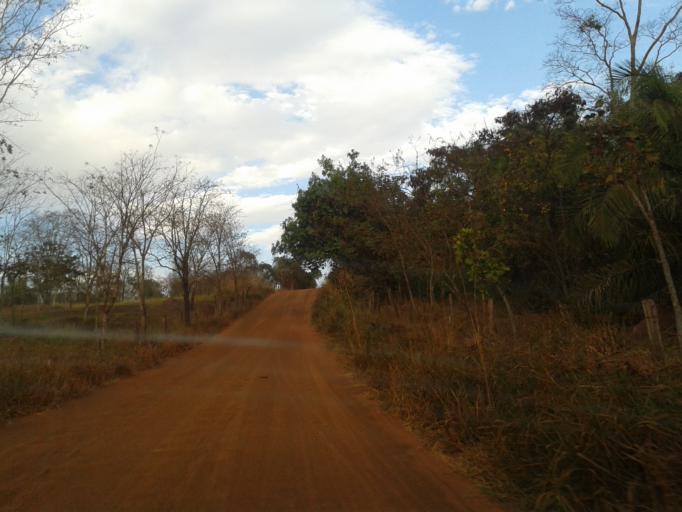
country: BR
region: Minas Gerais
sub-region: Ituiutaba
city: Ituiutaba
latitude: -19.1982
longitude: -49.8257
